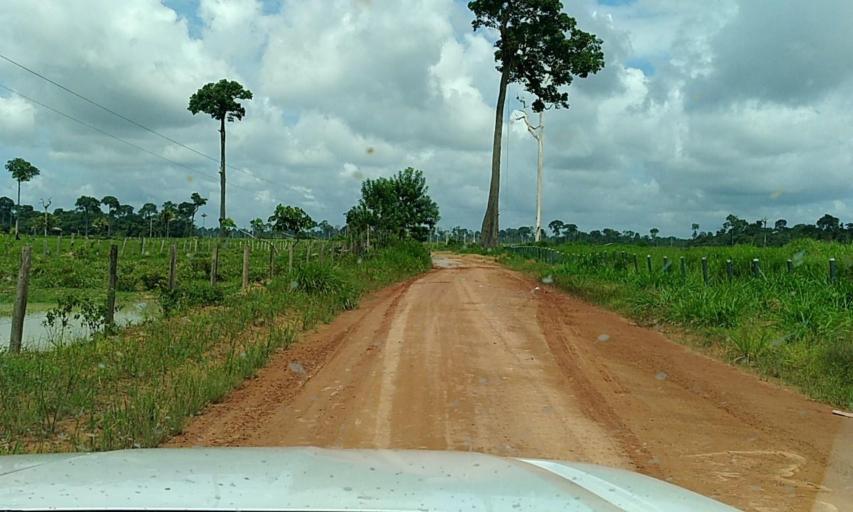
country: BR
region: Para
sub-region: Senador Jose Porfirio
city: Senador Jose Porfirio
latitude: -2.5172
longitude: -51.8475
